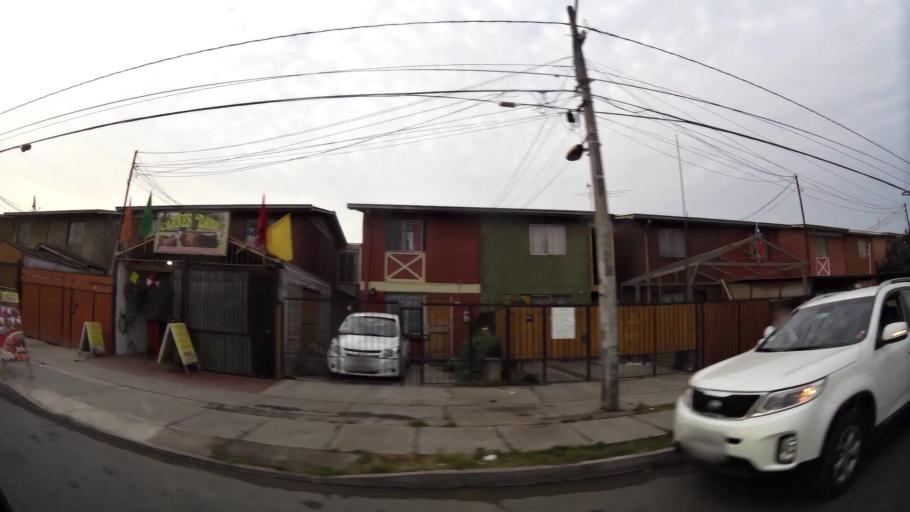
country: CL
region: Santiago Metropolitan
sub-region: Provincia de Santiago
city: Lo Prado
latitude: -33.5198
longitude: -70.7958
